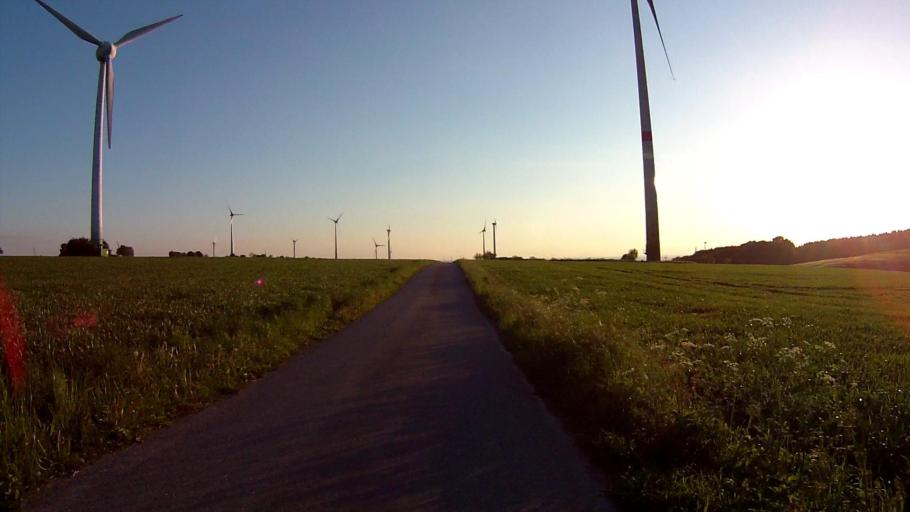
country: DE
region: North Rhine-Westphalia
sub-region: Regierungsbezirk Detmold
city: Altenbeken
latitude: 51.7261
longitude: 8.8875
